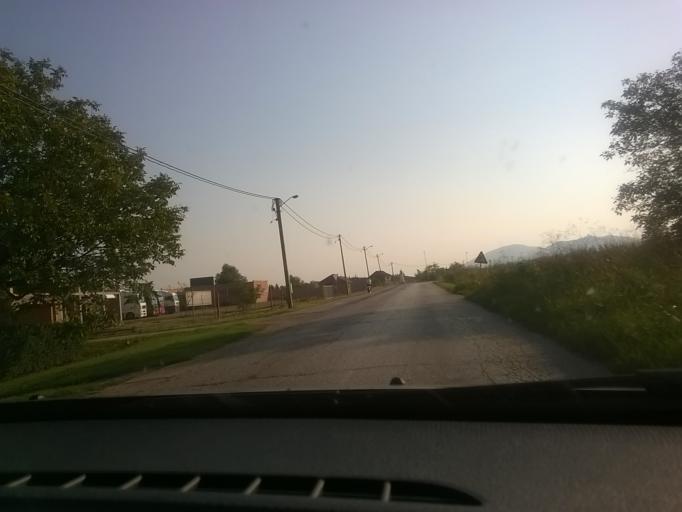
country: RS
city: Pavlis
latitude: 45.1110
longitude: 21.2508
